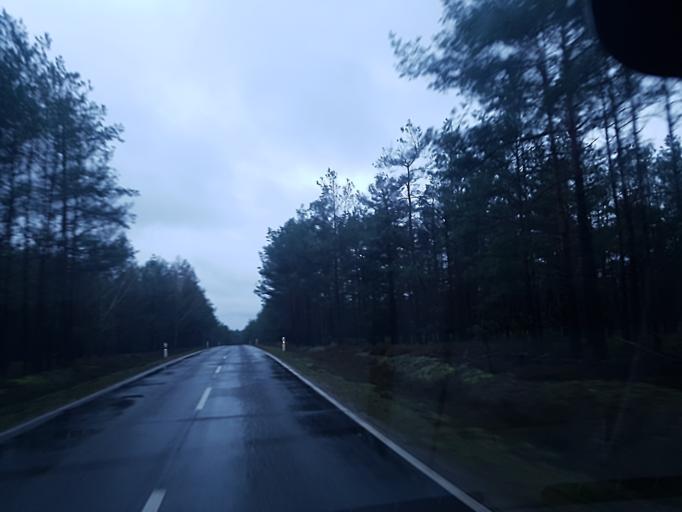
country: DE
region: Brandenburg
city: Schonewalde
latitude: 51.6159
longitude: 13.6355
